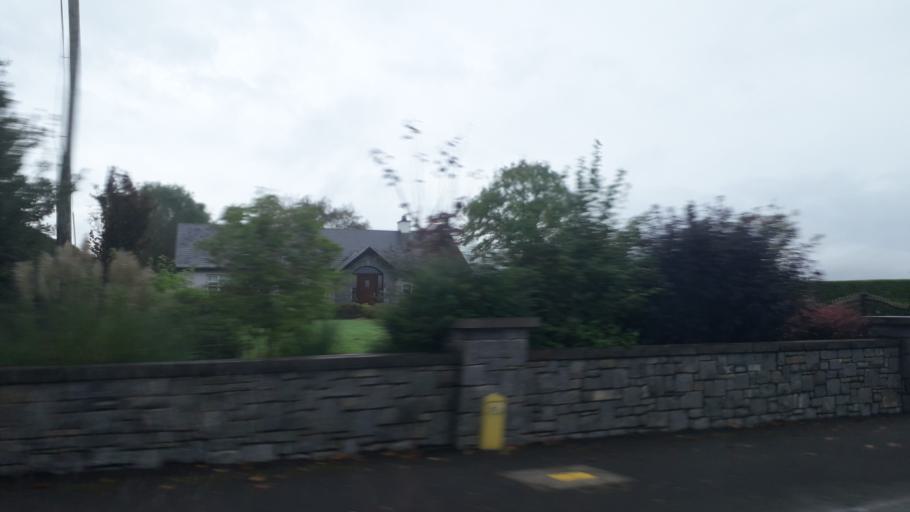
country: IE
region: Leinster
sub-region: An Longfort
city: Lanesborough
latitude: 53.7451
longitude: -7.9336
